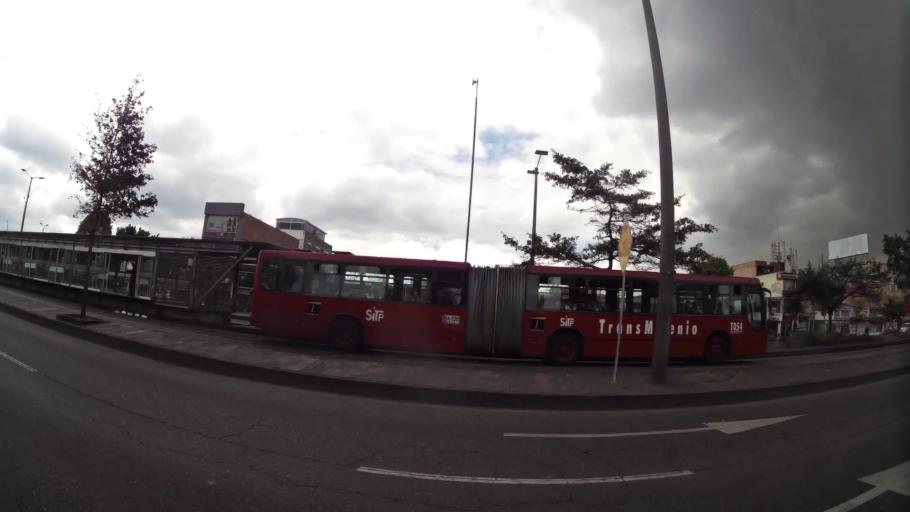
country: CO
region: Bogota D.C.
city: Barrio San Luis
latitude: 4.6913
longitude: -74.0847
